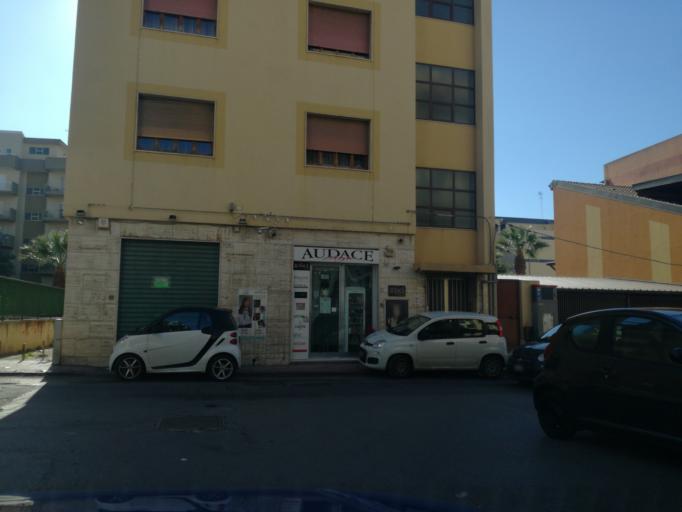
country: IT
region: Sicily
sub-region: Provincia di Caltanissetta
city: Gela
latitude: 37.0717
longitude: 14.2312
